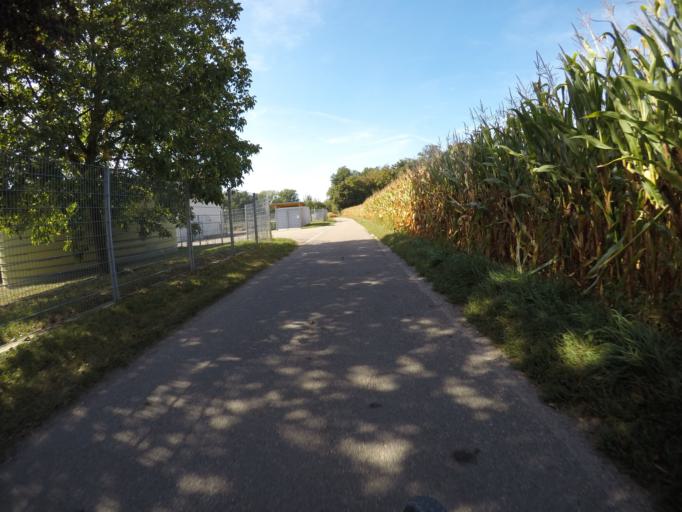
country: DE
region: Baden-Wuerttemberg
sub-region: Karlsruhe Region
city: Ubstadt-Weiher
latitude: 49.1526
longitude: 8.6520
